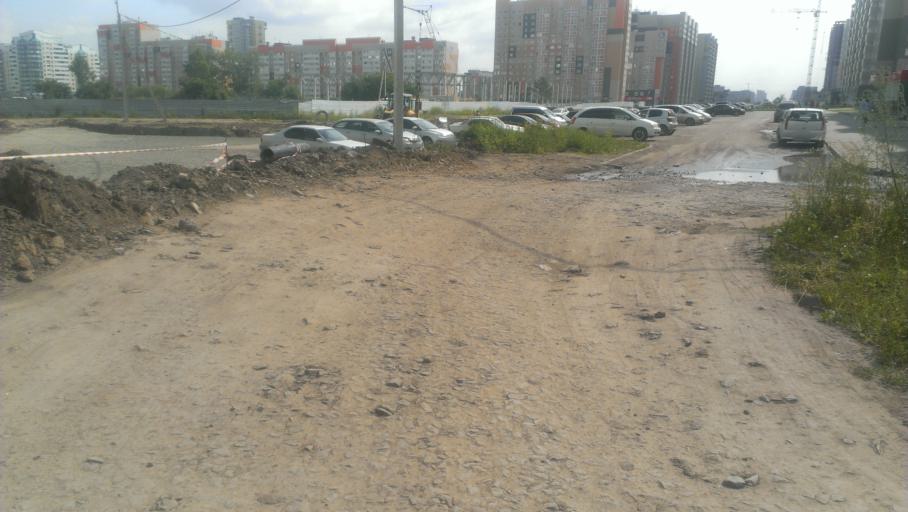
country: RU
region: Altai Krai
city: Novosilikatnyy
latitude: 53.3380
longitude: 83.6487
